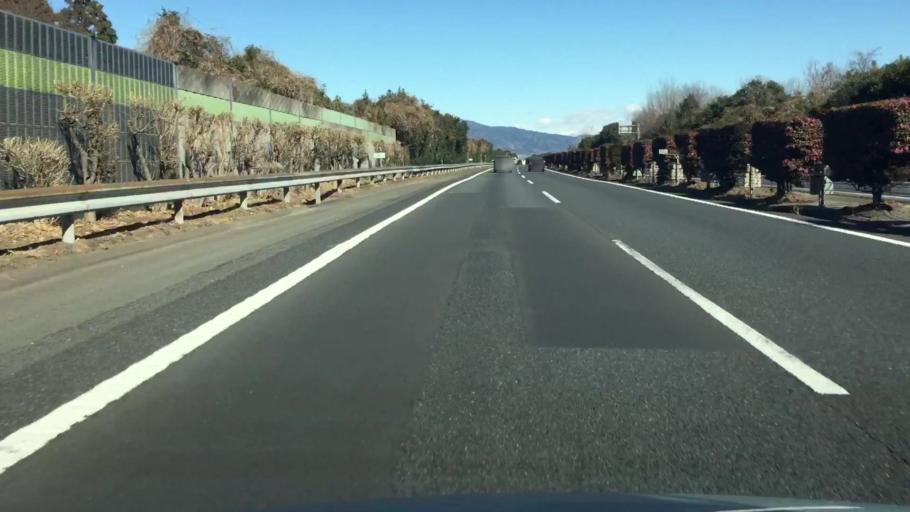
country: JP
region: Gunma
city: Kanekomachi
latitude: 36.4393
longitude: 139.0143
